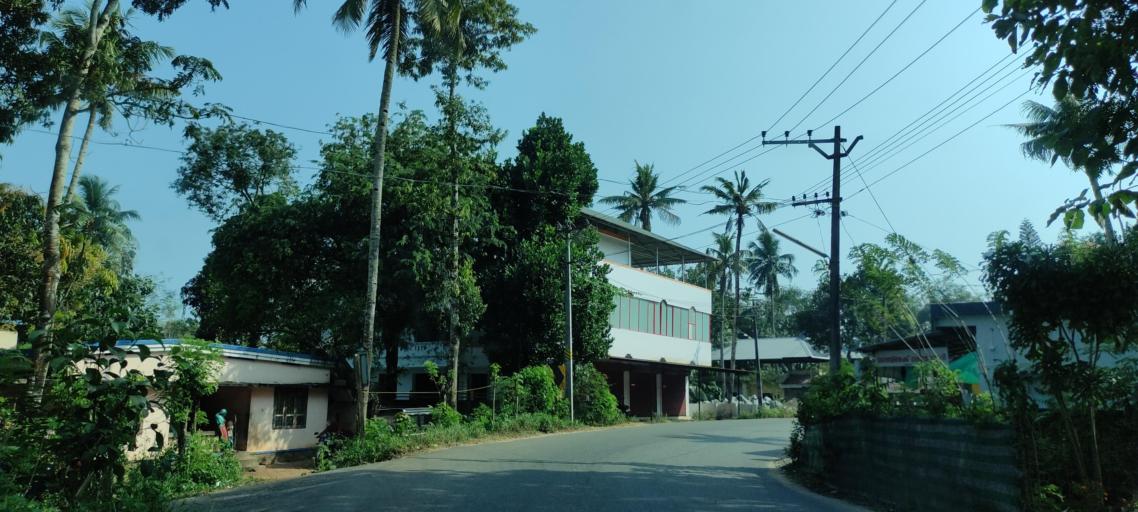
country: IN
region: Kerala
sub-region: Kollam
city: Panmana
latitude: 9.0472
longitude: 76.5753
